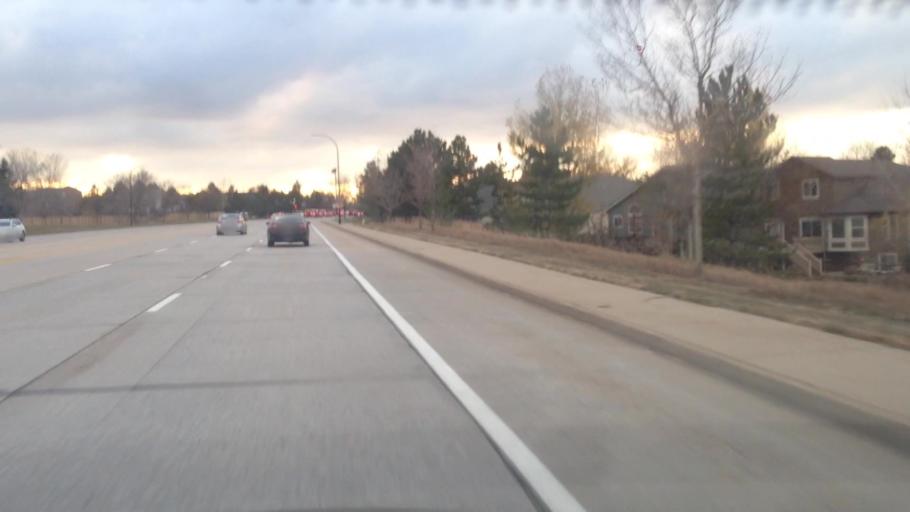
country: US
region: Colorado
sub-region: Douglas County
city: Carriage Club
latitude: 39.5434
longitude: -104.9271
